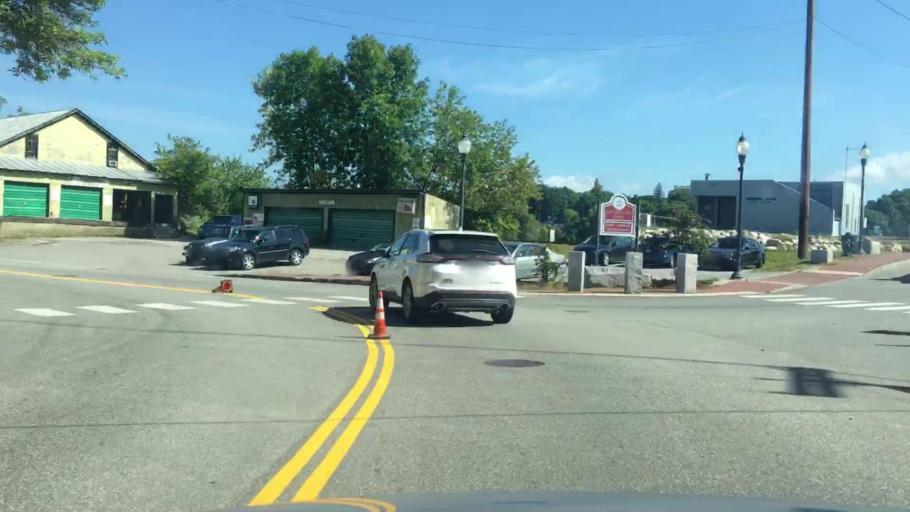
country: US
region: Maine
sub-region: Kennebec County
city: Gardiner
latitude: 44.2297
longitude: -69.7713
